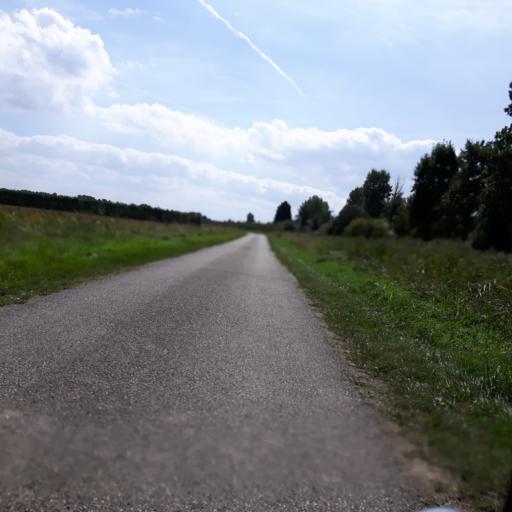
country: NL
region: Zeeland
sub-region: Gemeente Goes
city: Goes
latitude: 51.4685
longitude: 3.8971
